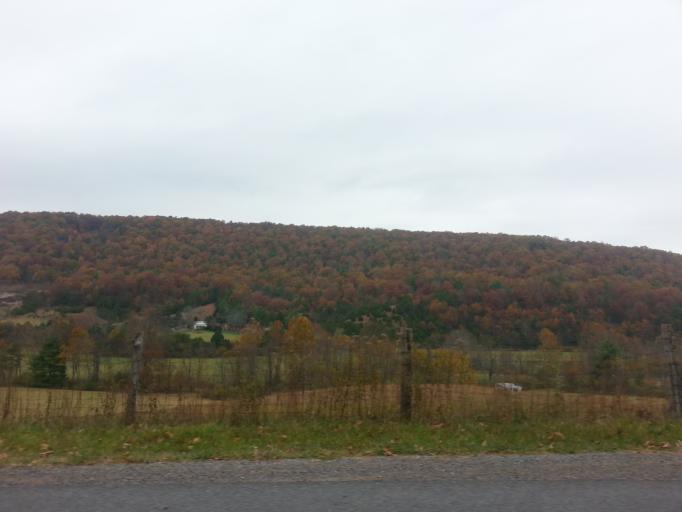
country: US
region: Virginia
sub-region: Pulaski County
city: Pulaski
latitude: 37.0812
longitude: -80.9372
